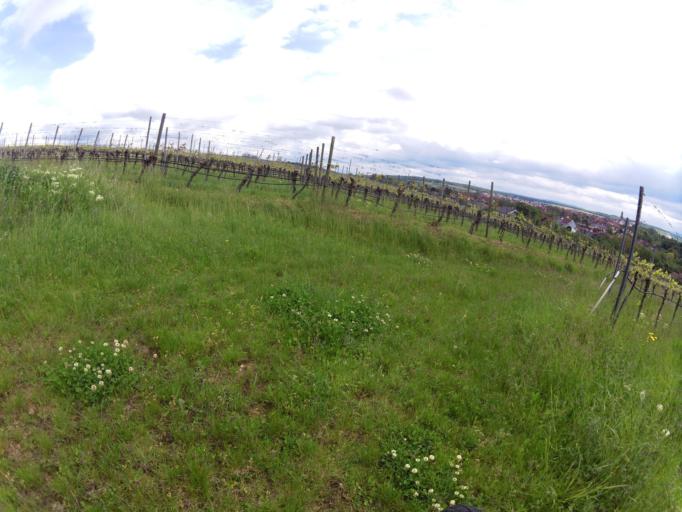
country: DE
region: Bavaria
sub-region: Regierungsbezirk Unterfranken
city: Volkach
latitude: 49.8737
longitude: 10.2178
